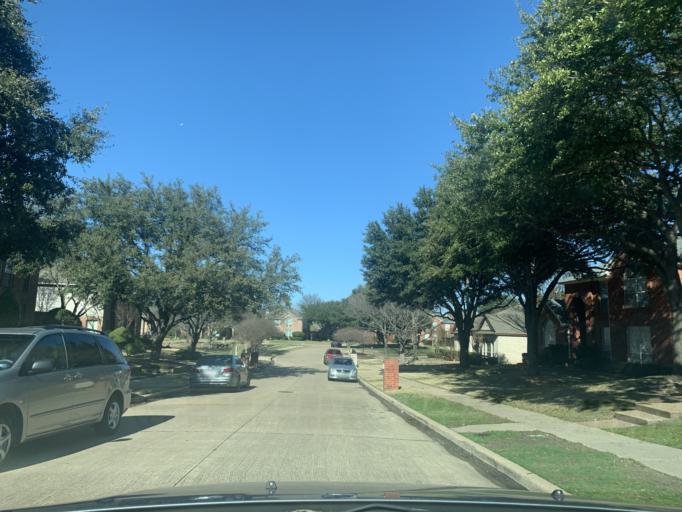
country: US
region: Texas
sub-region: Denton County
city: The Colony
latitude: 33.0607
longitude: -96.8348
